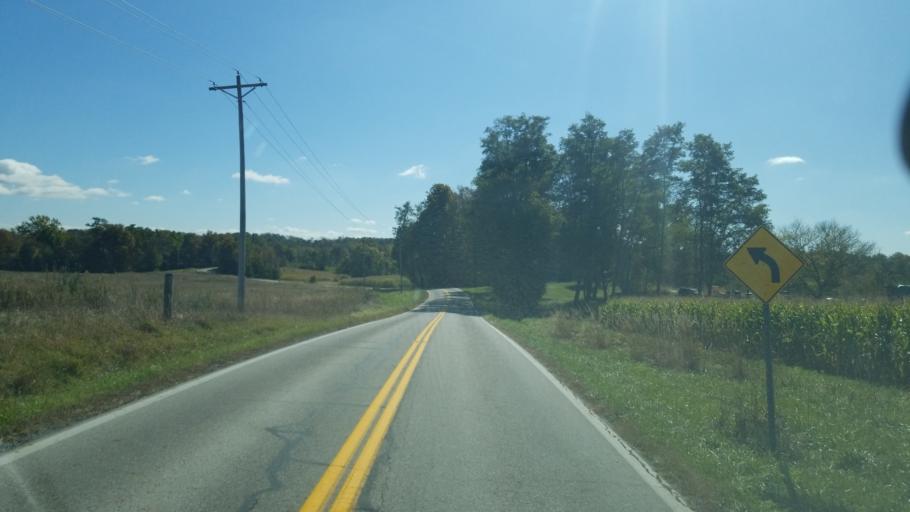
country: US
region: Ohio
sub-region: Highland County
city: Leesburg
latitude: 39.2764
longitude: -83.4880
